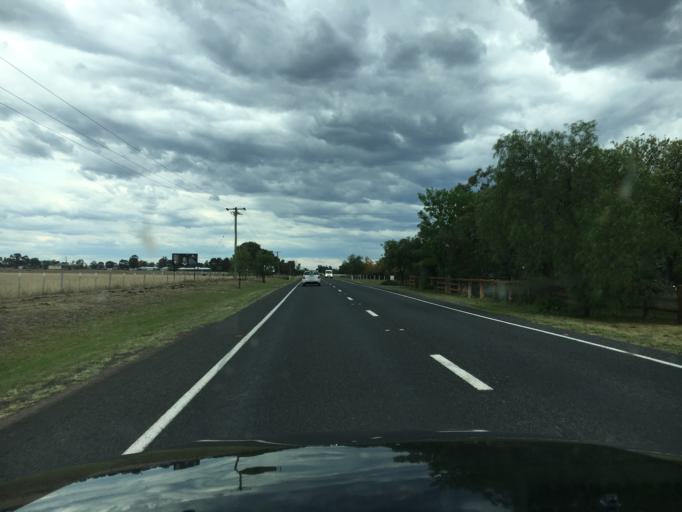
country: AU
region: New South Wales
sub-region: Muswellbrook
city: Muswellbrook
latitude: -32.0131
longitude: 150.8637
